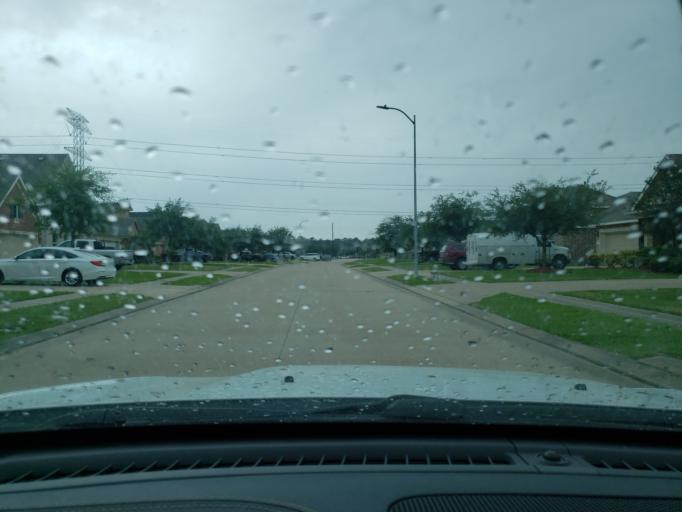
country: US
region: Texas
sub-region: Chambers County
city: Mont Belvieu
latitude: 29.8053
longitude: -94.9063
